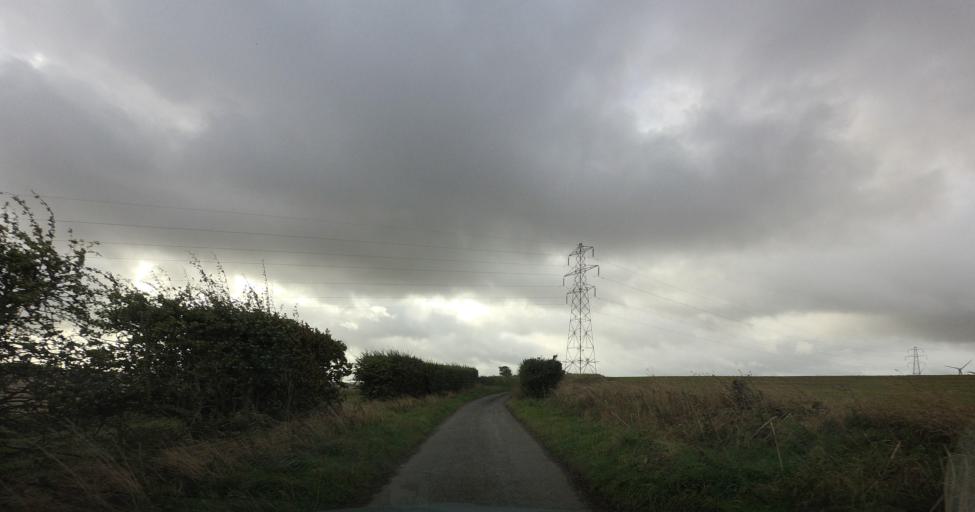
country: GB
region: Scotland
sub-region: Aberdeenshire
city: Whitehills
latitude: 57.6585
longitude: -2.6112
